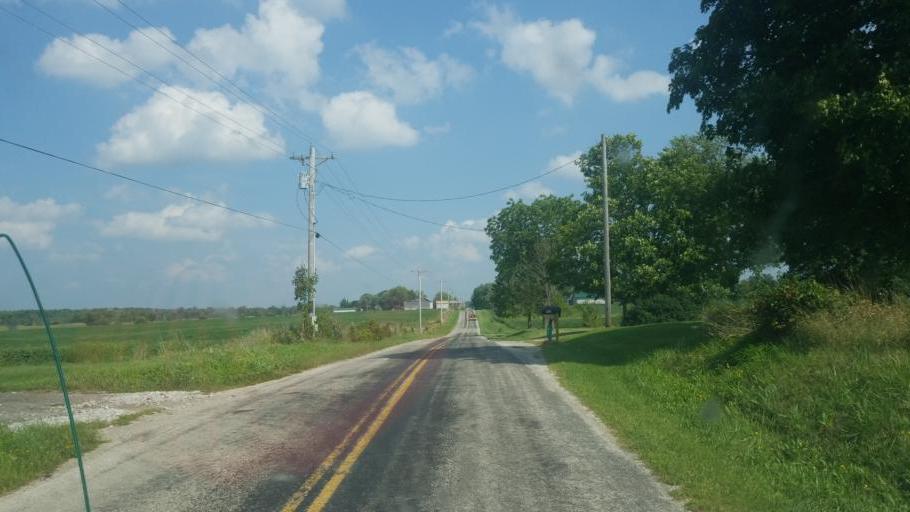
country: US
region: Ohio
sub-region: Huron County
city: New London
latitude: 41.0578
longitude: -82.2878
